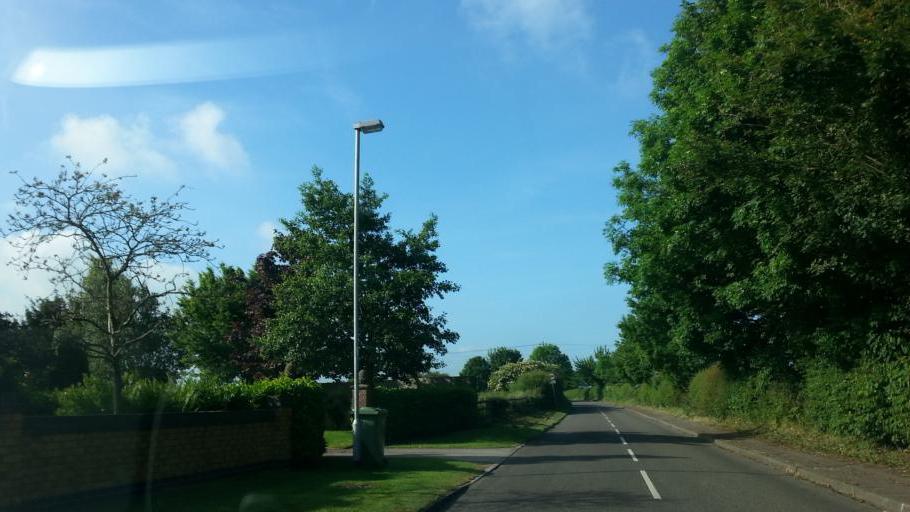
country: GB
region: England
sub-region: Nottinghamshire
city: Newark on Trent
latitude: 53.0598
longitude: -0.8256
